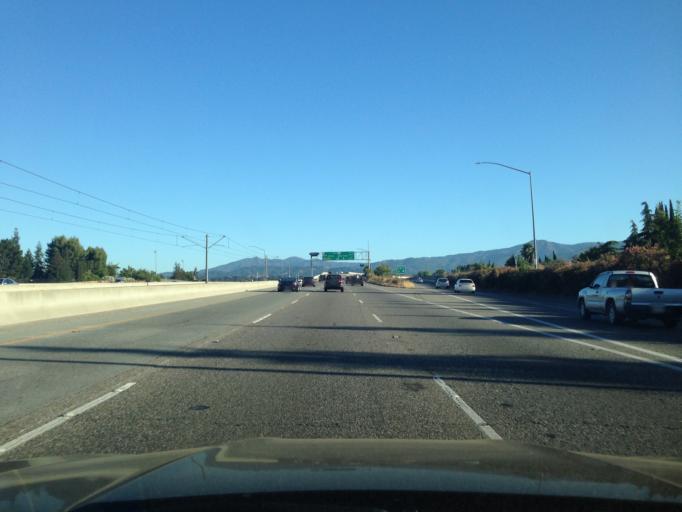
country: US
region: California
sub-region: Santa Clara County
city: Seven Trees
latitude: 37.2624
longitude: -121.8591
